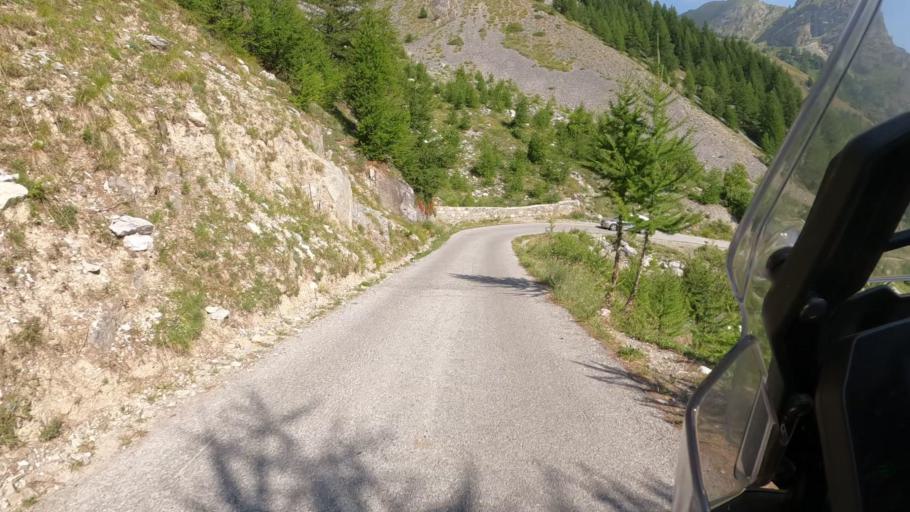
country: IT
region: Piedmont
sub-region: Provincia di Cuneo
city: Canosio
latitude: 44.4103
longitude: 7.0354
